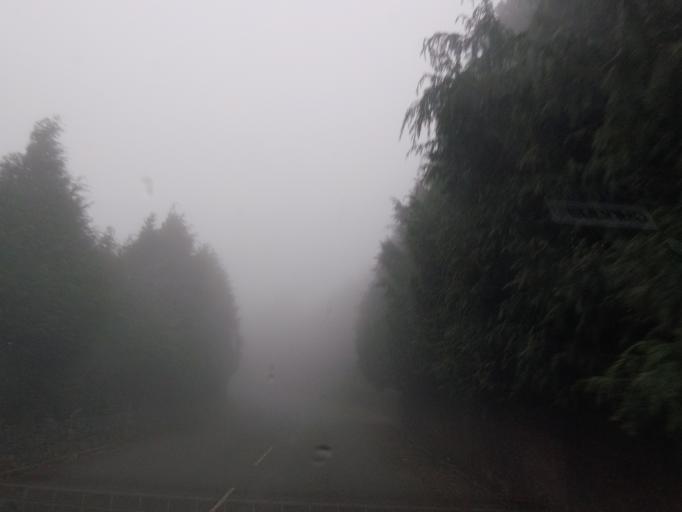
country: PT
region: Madeira
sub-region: Santa Cruz
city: Santa Cruz
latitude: 32.7213
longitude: -16.8098
